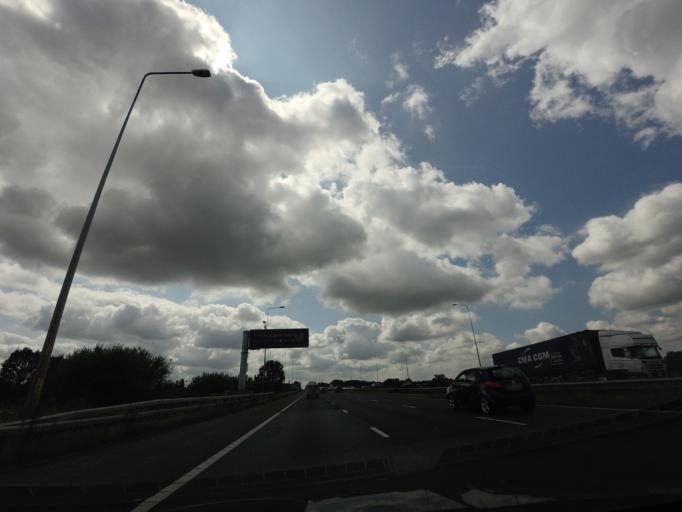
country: GB
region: England
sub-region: Borough of Wigan
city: Shevington
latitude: 53.6028
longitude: -2.6906
